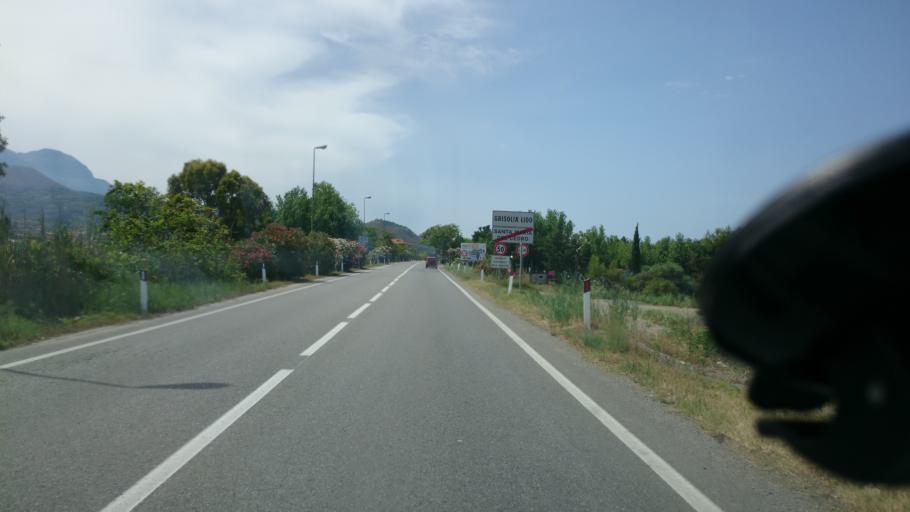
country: IT
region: Calabria
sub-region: Provincia di Cosenza
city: Marcellina
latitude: 39.7447
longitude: 15.8075
